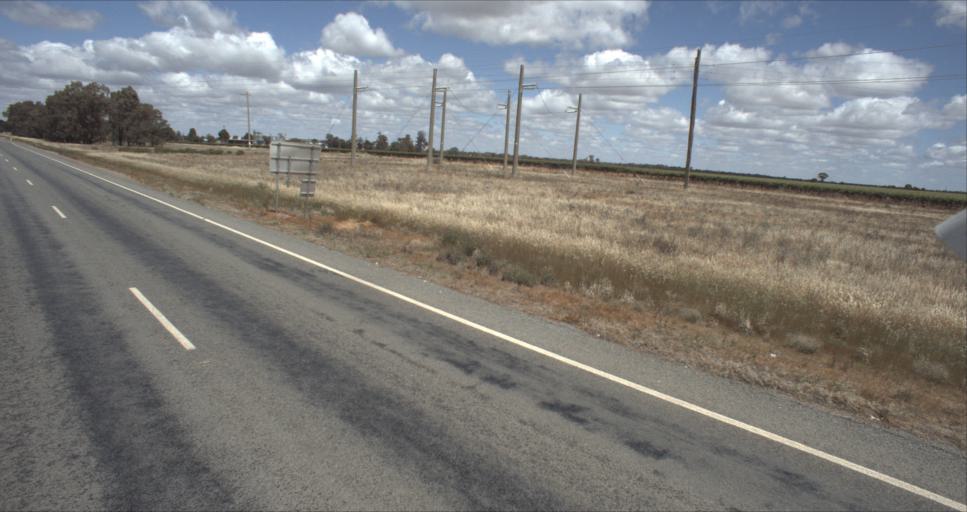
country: AU
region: New South Wales
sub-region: Murrumbidgee Shire
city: Darlington Point
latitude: -34.5050
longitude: 146.1874
